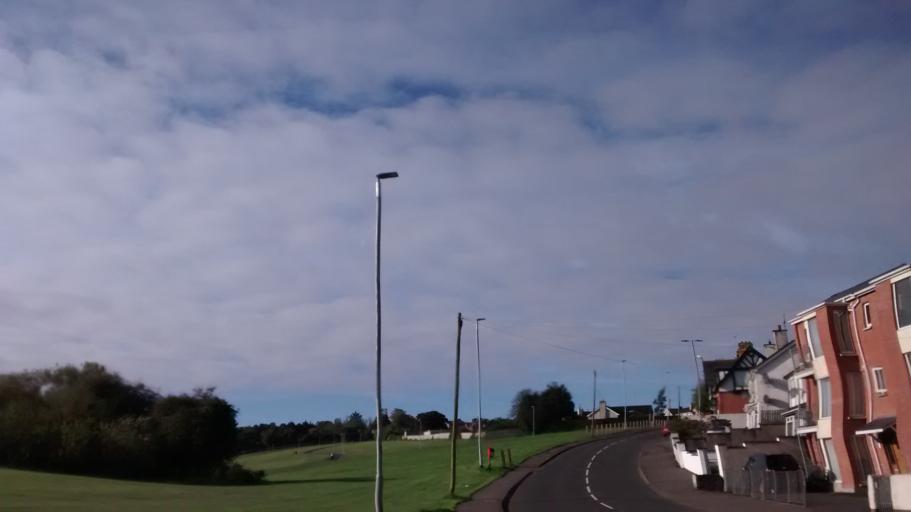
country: GB
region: Northern Ireland
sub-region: City of Derry
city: Derry
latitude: 55.0083
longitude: -7.3307
